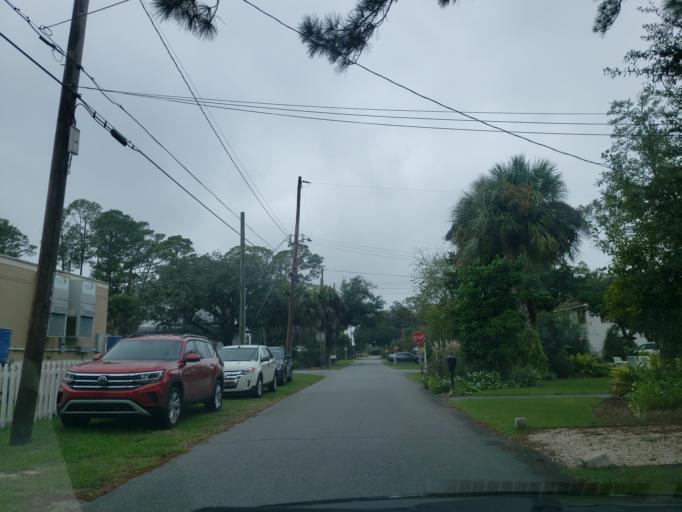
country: US
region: Georgia
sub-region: Chatham County
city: Tybee Island
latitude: 32.0040
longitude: -80.8457
